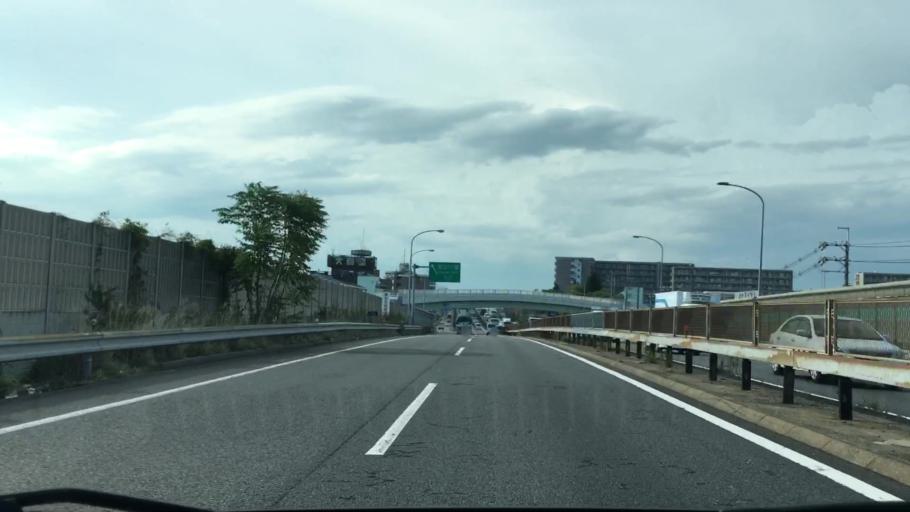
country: JP
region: Hyogo
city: Kakogawacho-honmachi
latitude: 34.7457
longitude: 134.8725
